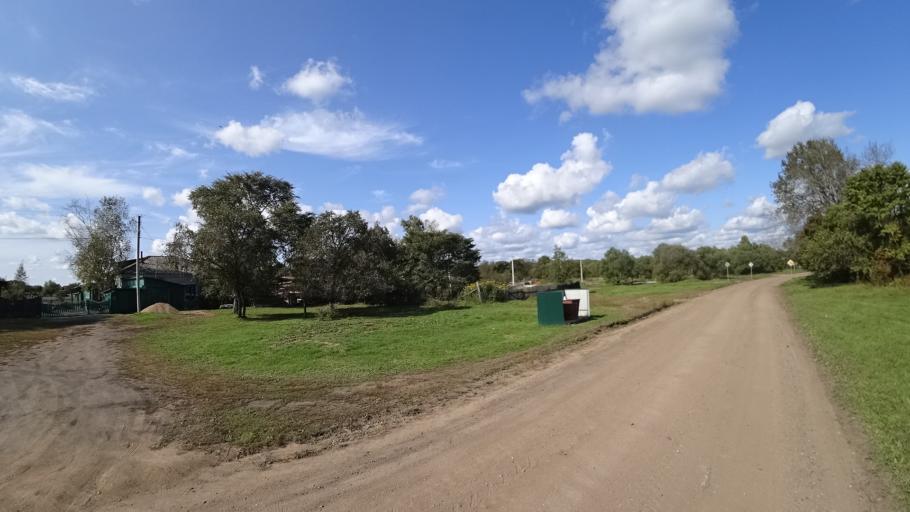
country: RU
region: Amur
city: Arkhara
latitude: 49.4054
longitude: 130.1567
